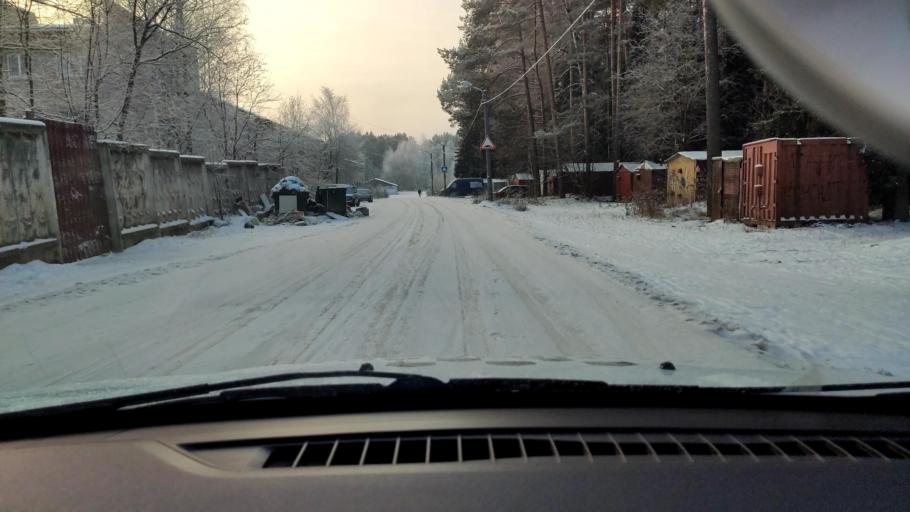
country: RU
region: Perm
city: Kondratovo
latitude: 58.0458
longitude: 56.1383
